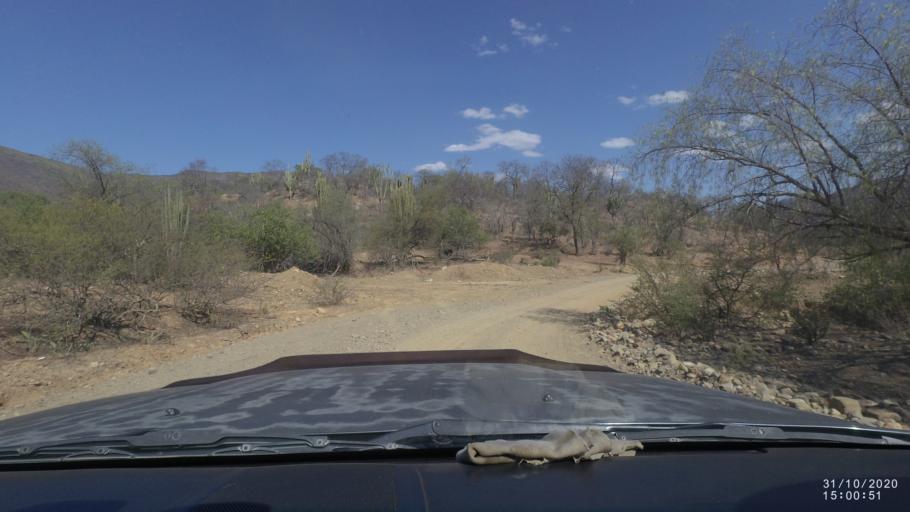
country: BO
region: Cochabamba
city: Aiquile
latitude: -18.2599
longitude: -64.8221
